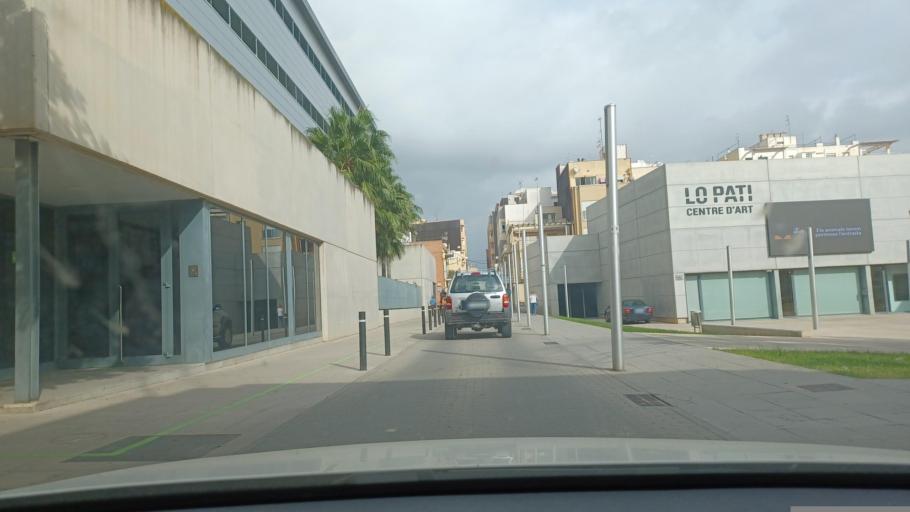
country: ES
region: Catalonia
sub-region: Provincia de Tarragona
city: Amposta
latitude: 40.7087
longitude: 0.5764
